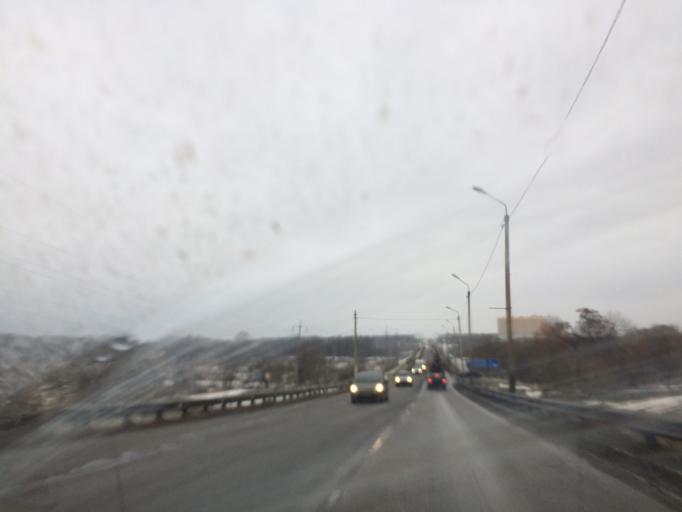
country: RU
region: Tula
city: Mendeleyevskiy
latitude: 54.1576
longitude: 37.5672
